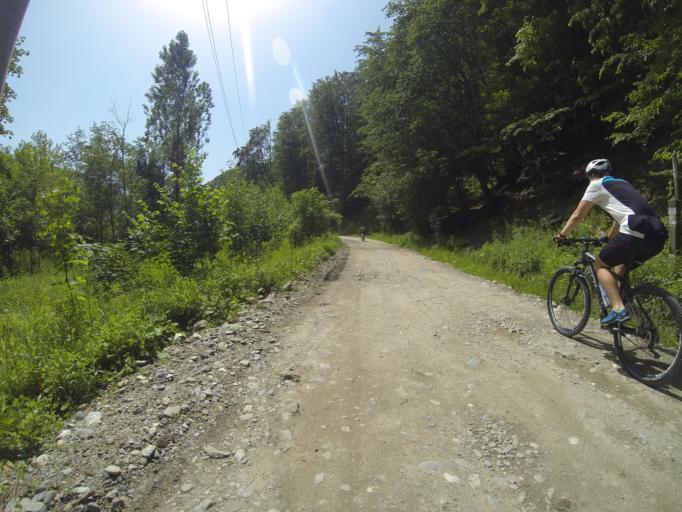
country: RO
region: Valcea
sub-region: Oras Baile Olanesti
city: Baile Olanesti
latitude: 45.2192
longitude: 24.2155
